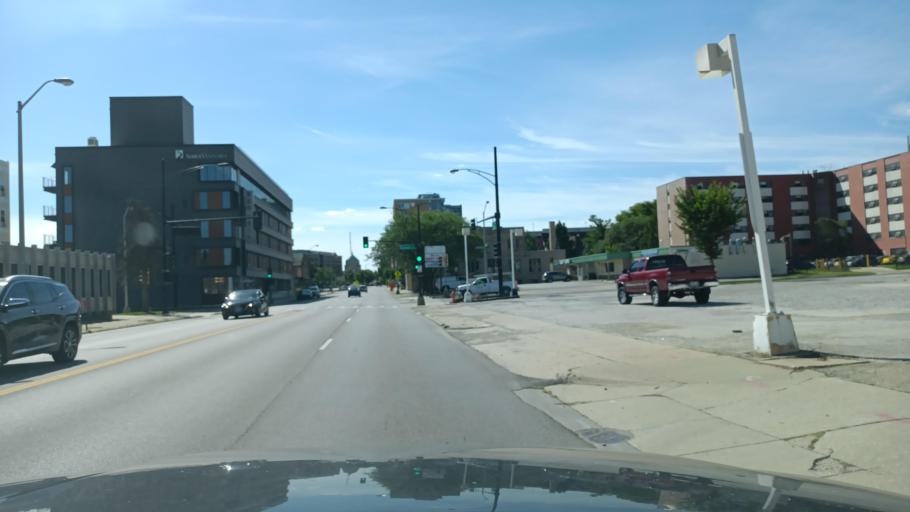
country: US
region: Illinois
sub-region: Champaign County
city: Champaign
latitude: 40.1218
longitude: -88.2436
